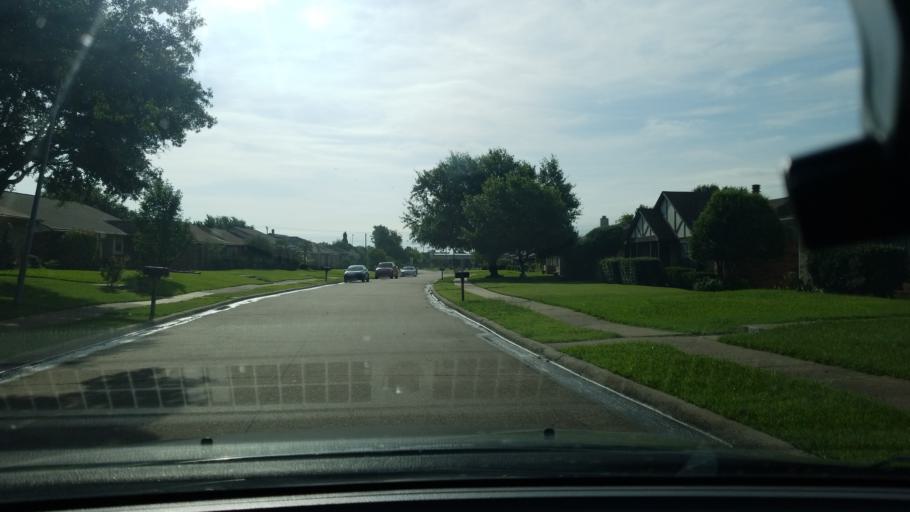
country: US
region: Texas
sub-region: Dallas County
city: Mesquite
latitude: 32.8029
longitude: -96.6132
